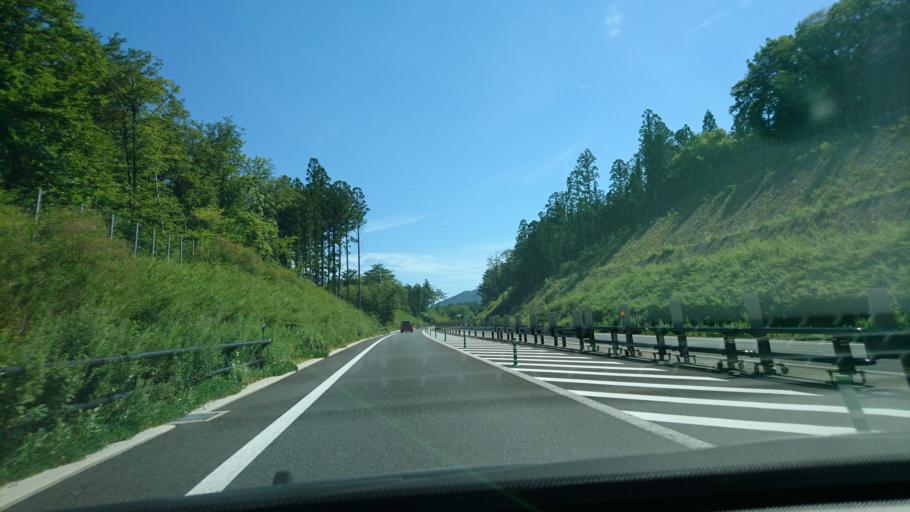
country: JP
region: Iwate
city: Tono
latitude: 39.2980
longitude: 141.4131
